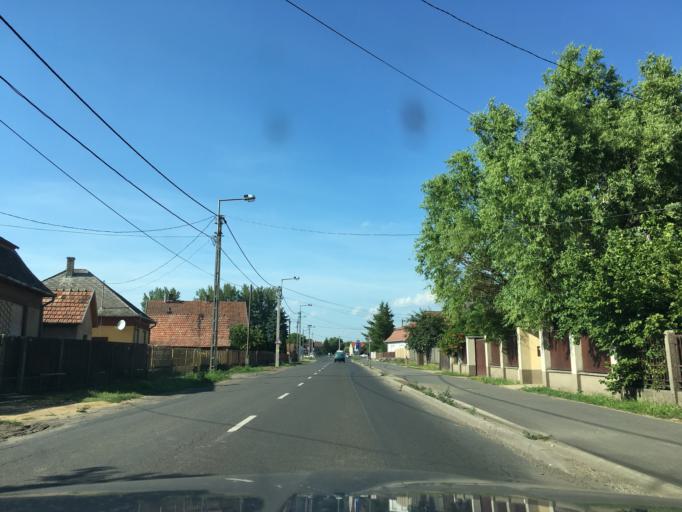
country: HU
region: Hajdu-Bihar
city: Hajdusamson
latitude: 47.6100
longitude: 21.7651
